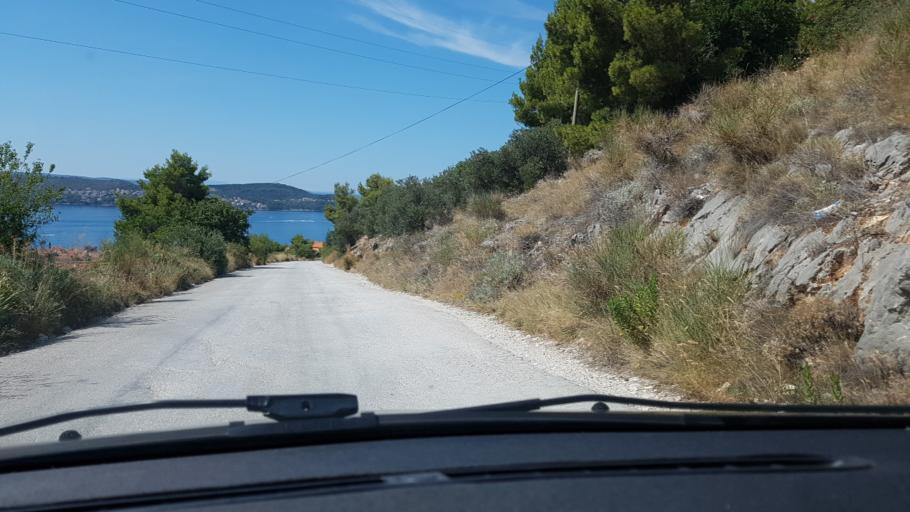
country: HR
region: Splitsko-Dalmatinska
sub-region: Grad Trogir
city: Trogir
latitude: 43.5272
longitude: 16.2286
